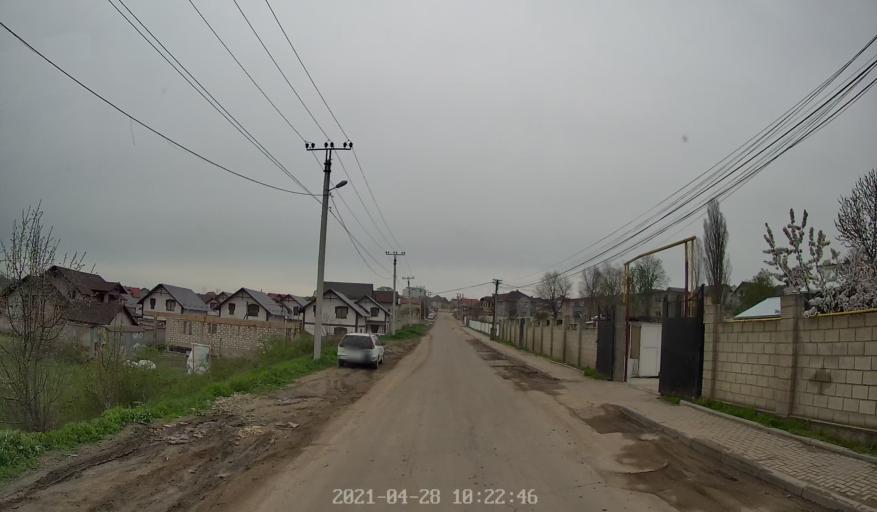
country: MD
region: Chisinau
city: Chisinau
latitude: 46.9932
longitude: 28.9347
